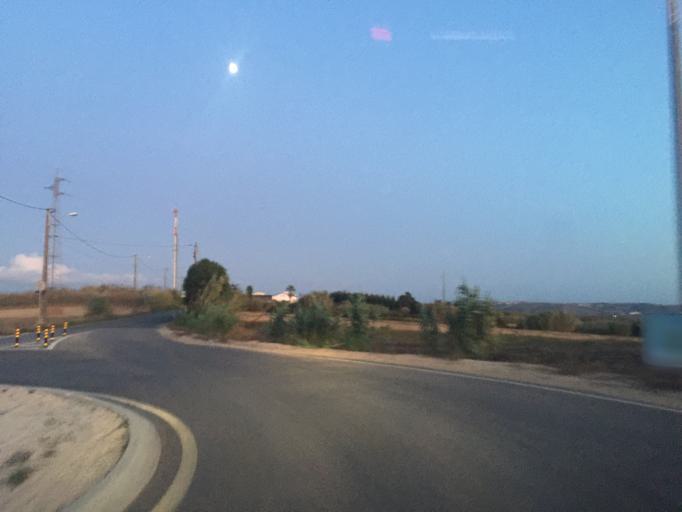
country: PT
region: Lisbon
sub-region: Lourinha
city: Lourinha
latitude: 39.2766
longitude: -9.2982
